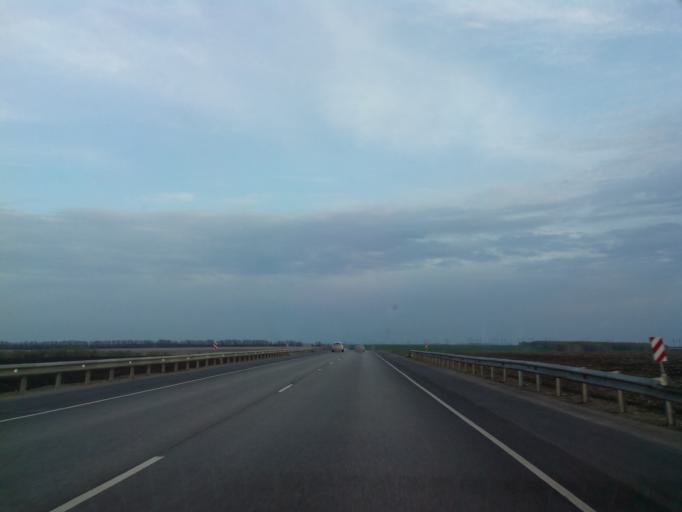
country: RU
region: Rjazan
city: Ryazhsk
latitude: 53.5647
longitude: 40.0497
